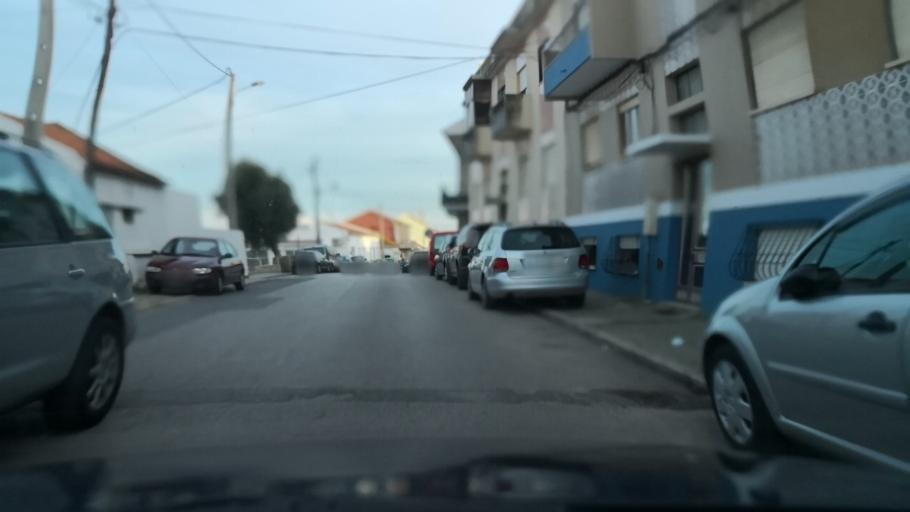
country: PT
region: Setubal
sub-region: Setubal
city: Setubal
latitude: 38.5271
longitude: -8.8658
